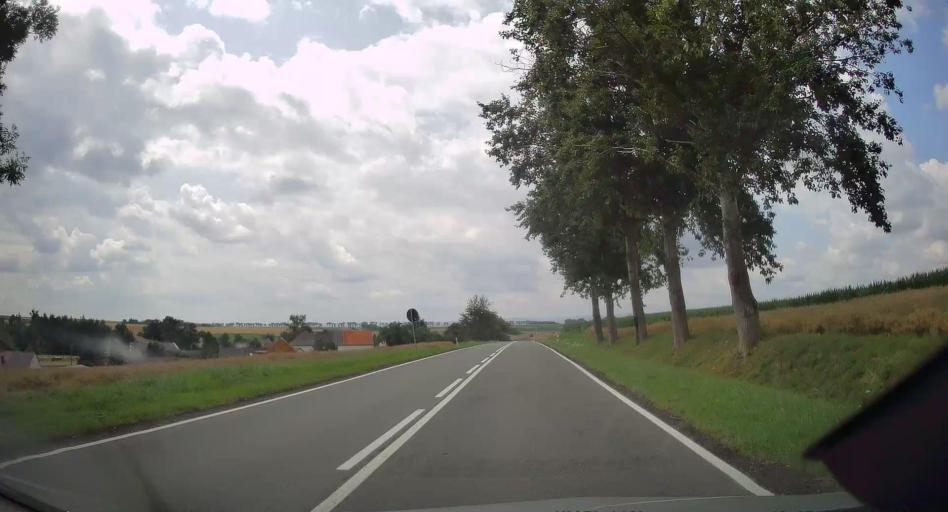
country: PL
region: Opole Voivodeship
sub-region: Powiat prudnicki
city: Raclawice Slaskie
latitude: 50.3437
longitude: 17.7347
